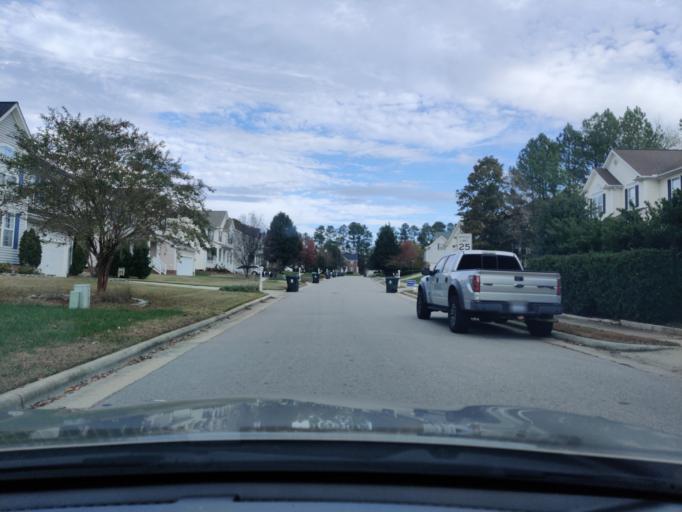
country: US
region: North Carolina
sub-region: Wake County
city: Morrisville
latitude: 35.8201
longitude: -78.8391
